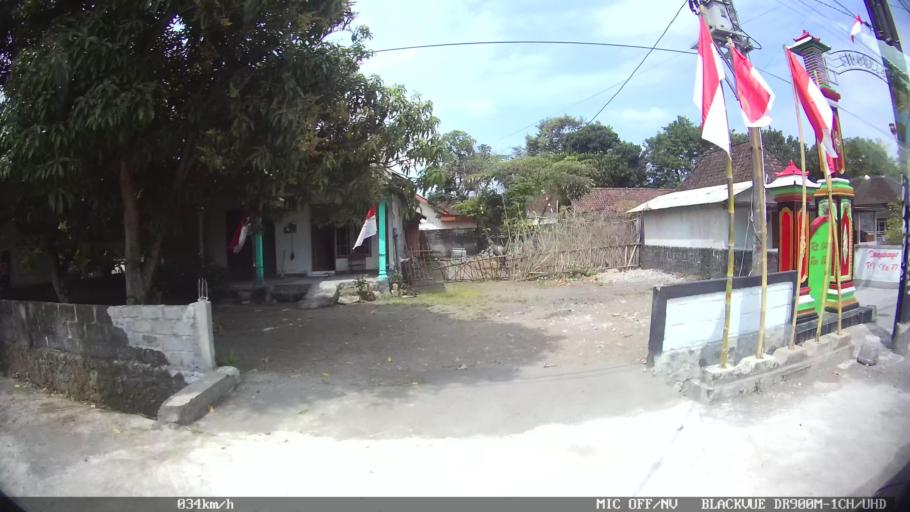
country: ID
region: Daerah Istimewa Yogyakarta
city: Depok
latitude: -7.7319
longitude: 110.4514
